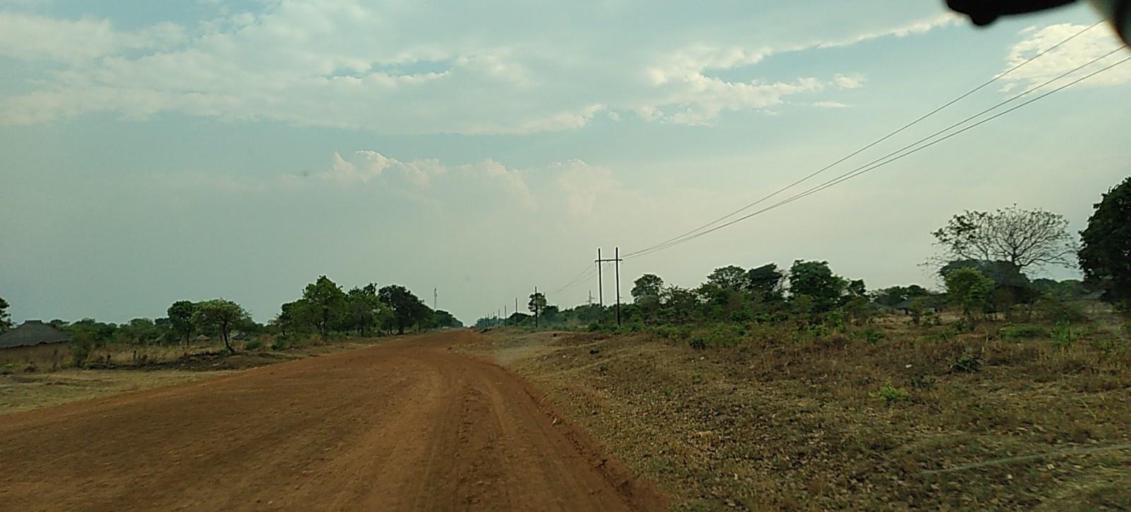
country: ZM
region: North-Western
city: Kabompo
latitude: -13.8726
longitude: 23.6673
